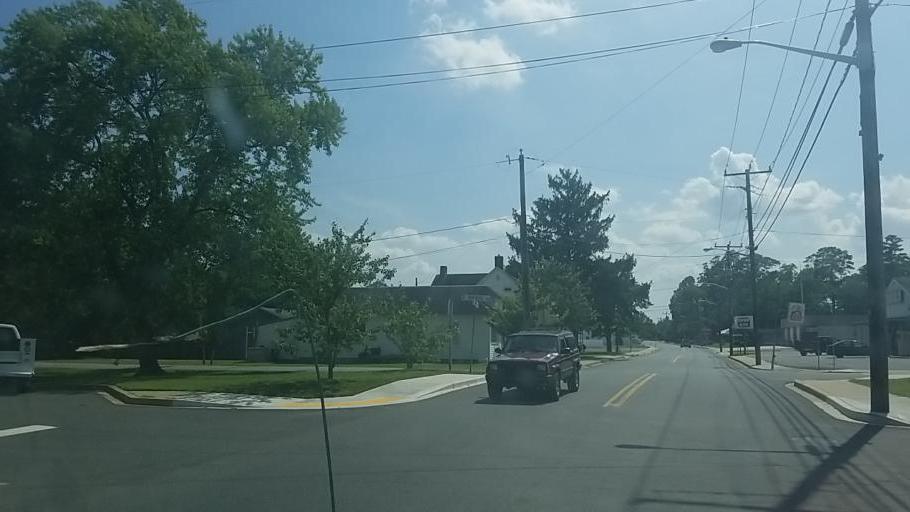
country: US
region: Maryland
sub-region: Wicomico County
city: Hebron
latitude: 38.4191
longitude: -75.6890
